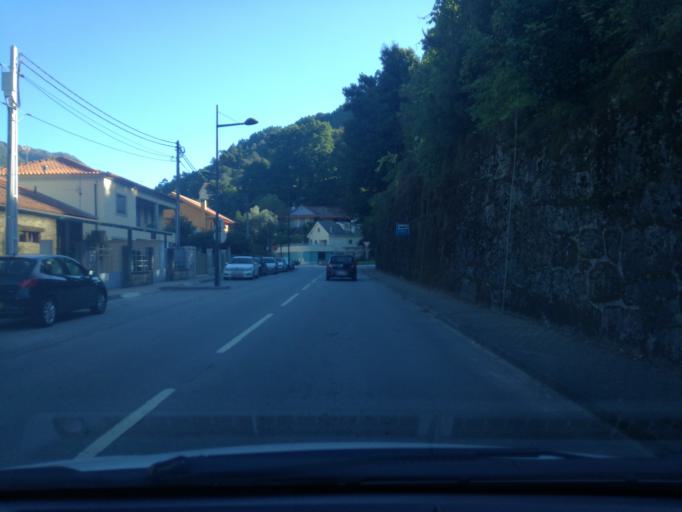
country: PT
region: Braga
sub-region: Vieira do Minho
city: Real
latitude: 41.7238
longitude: -8.1632
